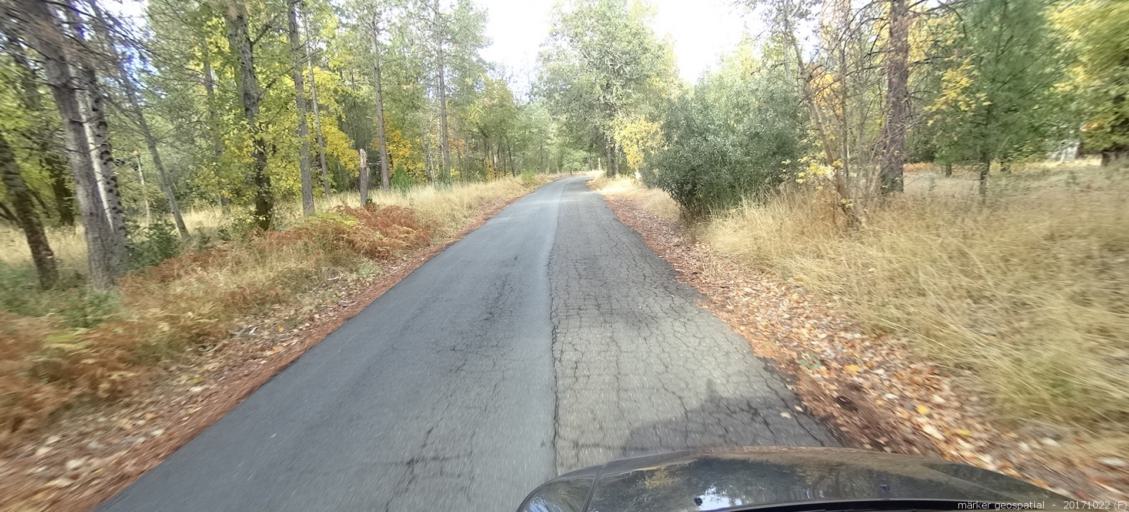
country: US
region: California
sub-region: Siskiyou County
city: Dunsmuir
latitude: 41.1527
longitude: -122.3407
